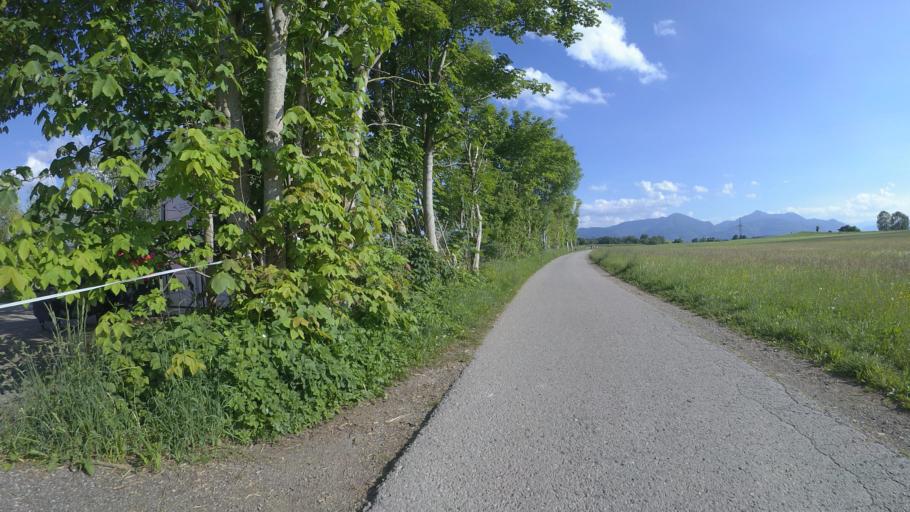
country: DE
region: Bavaria
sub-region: Upper Bavaria
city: Nussdorf
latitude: 47.8792
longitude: 12.5990
